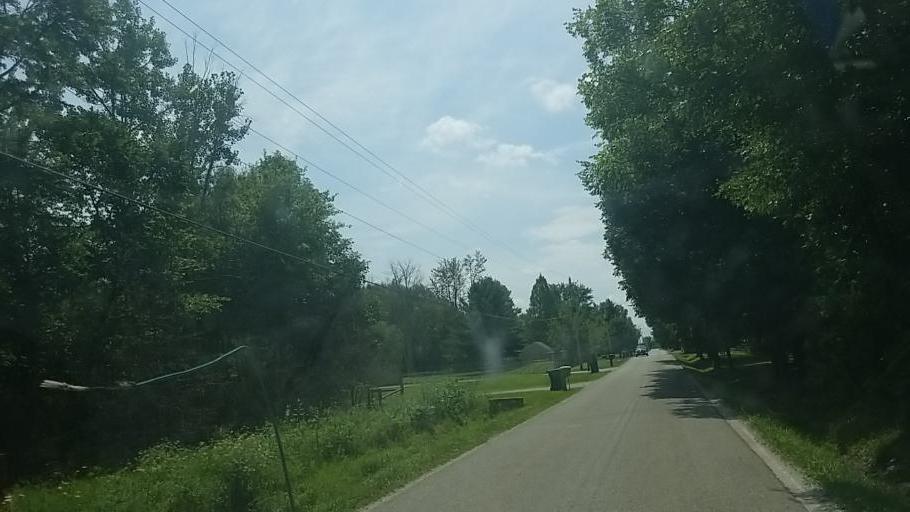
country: US
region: Ohio
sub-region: Franklin County
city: New Albany
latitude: 40.0342
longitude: -82.7689
